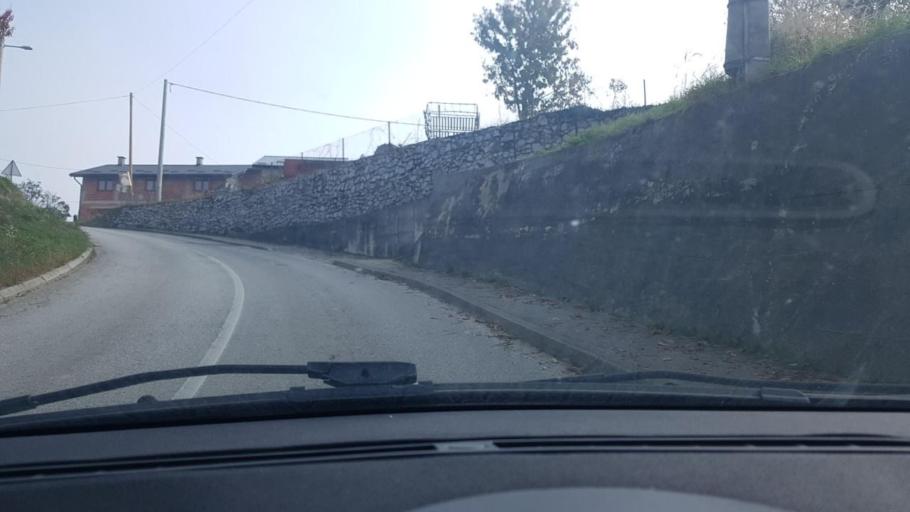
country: HR
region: Krapinsko-Zagorska
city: Zlatar
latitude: 46.1485
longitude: 16.0601
